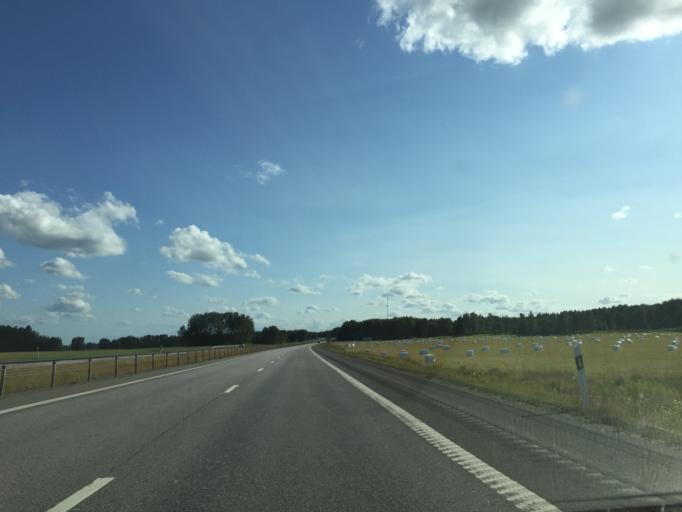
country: SE
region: OErebro
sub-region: Kumla Kommun
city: Kumla
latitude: 59.1497
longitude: 15.0963
